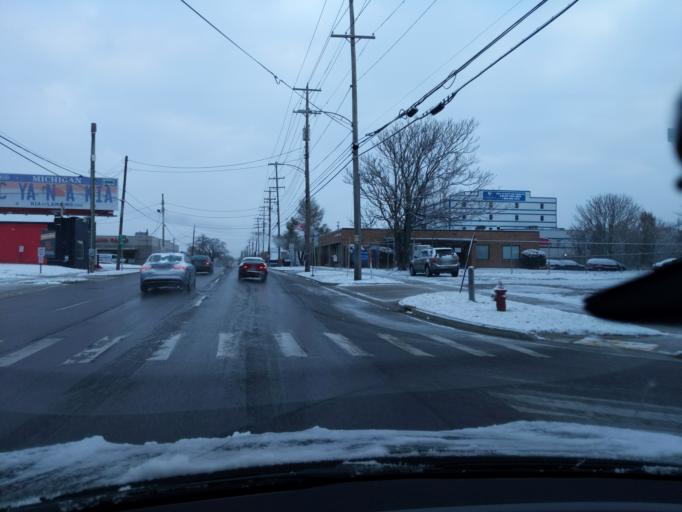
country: US
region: Michigan
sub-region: Ingham County
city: Lansing
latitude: 42.7372
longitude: -84.5446
